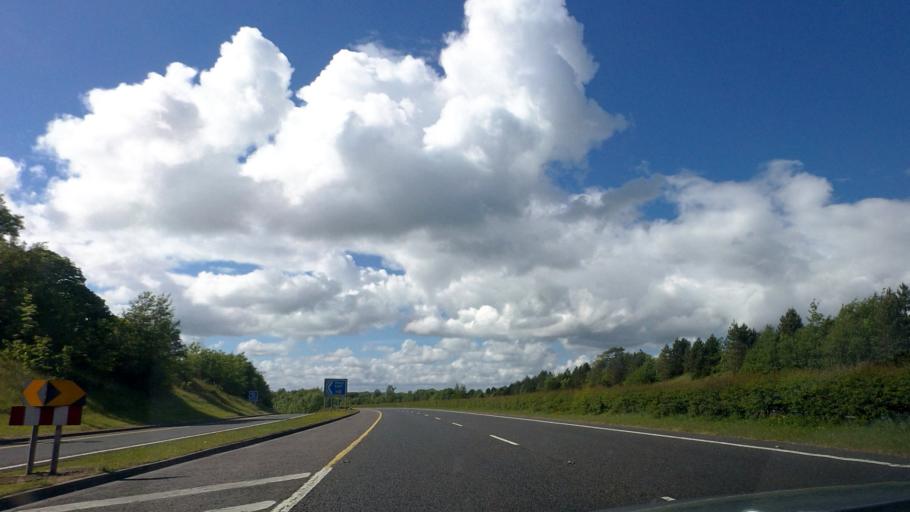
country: IE
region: Munster
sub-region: An Clar
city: Newmarket on Fergus
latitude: 52.7490
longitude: -8.8985
